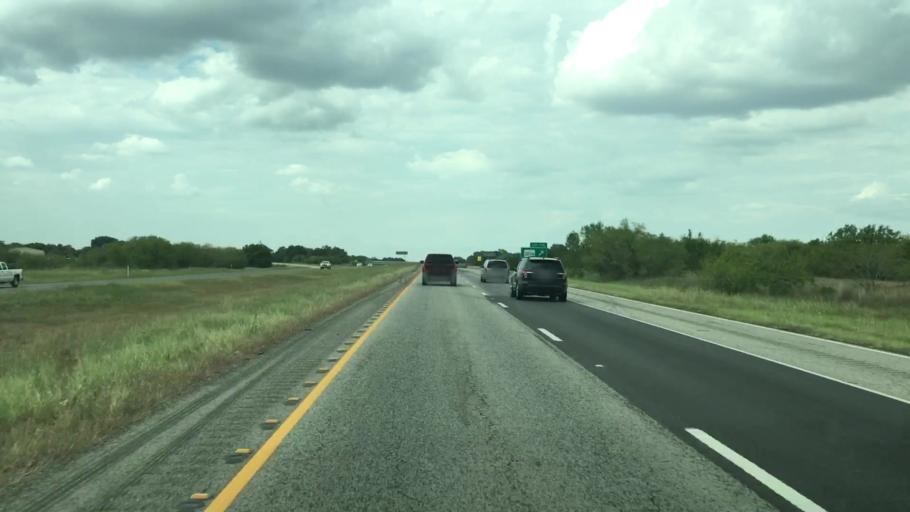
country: US
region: Texas
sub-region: Atascosa County
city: Pleasanton
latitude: 29.0451
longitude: -98.4315
